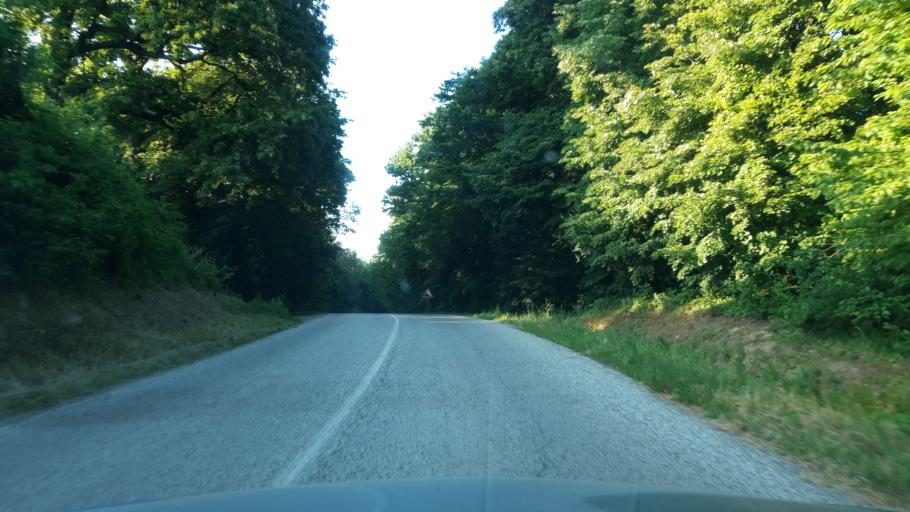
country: RS
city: Glozan
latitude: 45.1477
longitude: 19.5793
